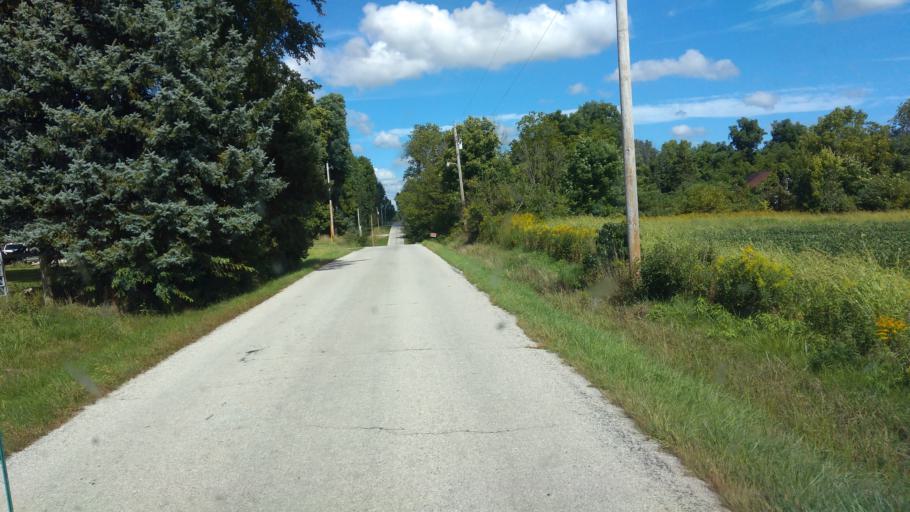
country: US
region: Ohio
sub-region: Huron County
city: Plymouth
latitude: 41.0213
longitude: -82.6515
